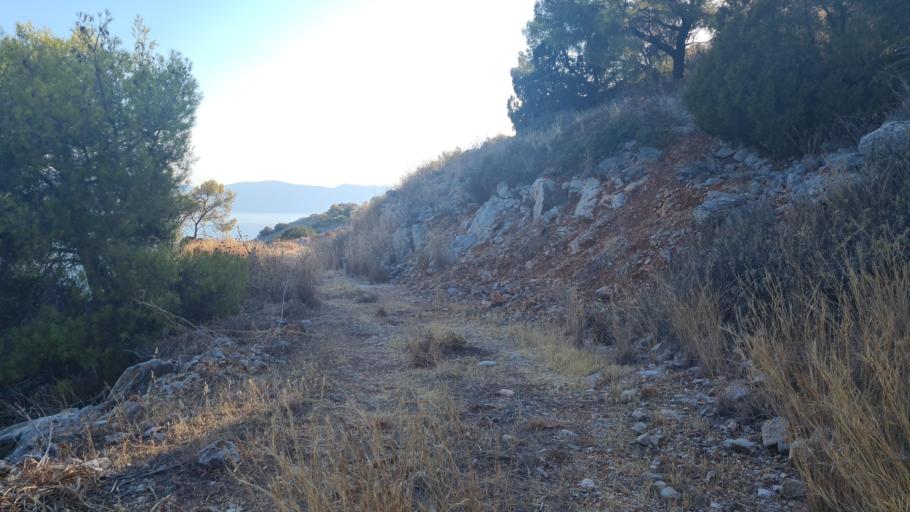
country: GR
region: Attica
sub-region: Nomos Piraios
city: Megalochori
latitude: 37.6916
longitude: 23.3604
